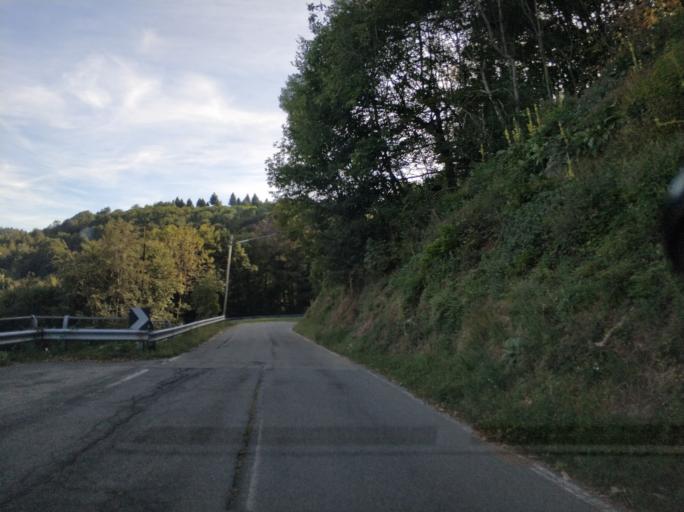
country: IT
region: Piedmont
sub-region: Provincia di Torino
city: Monastero di Lanzo
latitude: 45.3021
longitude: 7.4291
